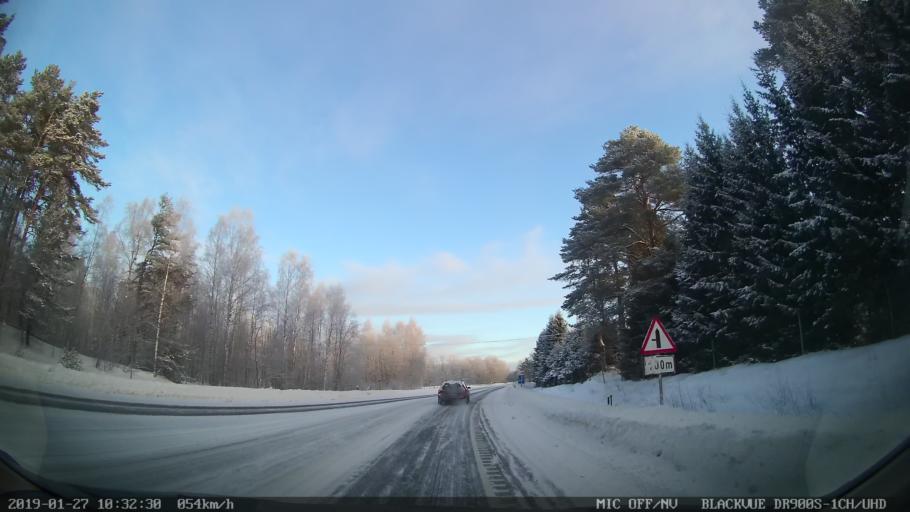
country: EE
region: Harju
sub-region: Raasiku vald
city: Raasiku
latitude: 59.4406
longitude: 25.1871
